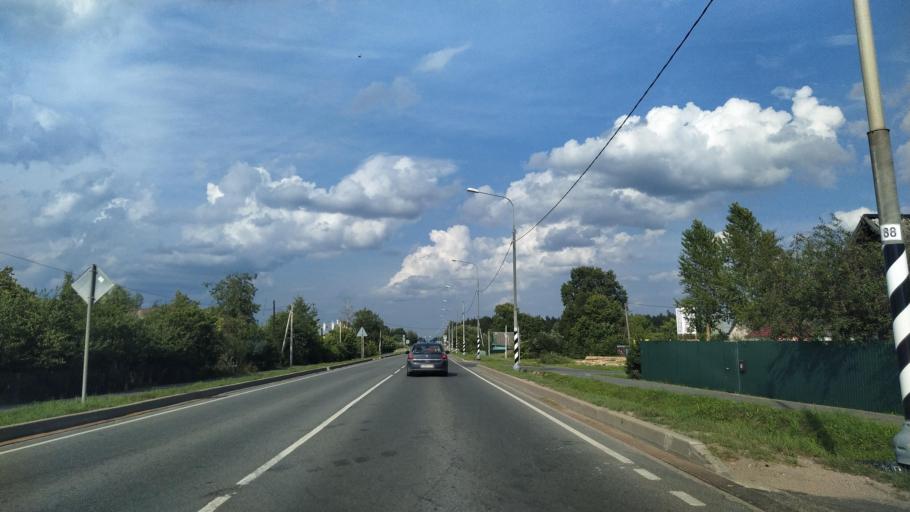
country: RU
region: Novgorod
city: Shimsk
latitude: 58.2119
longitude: 30.7245
